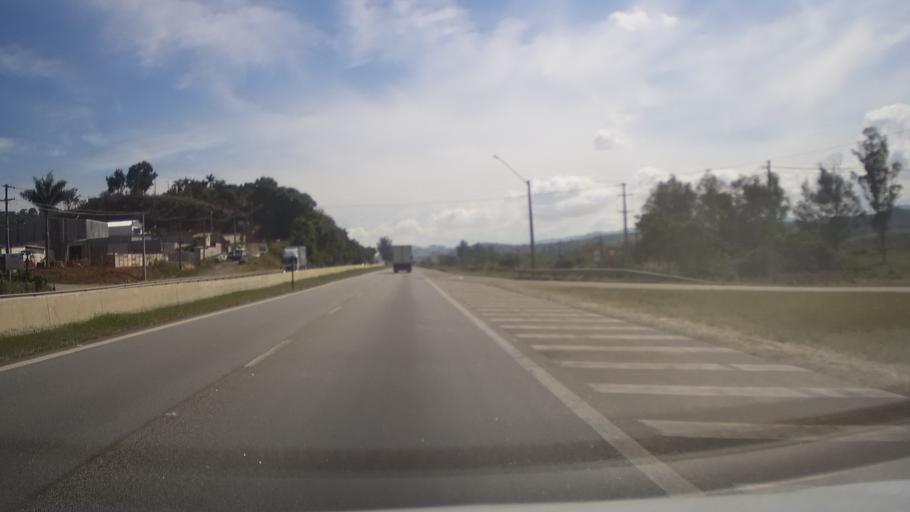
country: BR
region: Minas Gerais
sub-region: Cambui
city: Cambui
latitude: -22.5935
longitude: -46.0548
